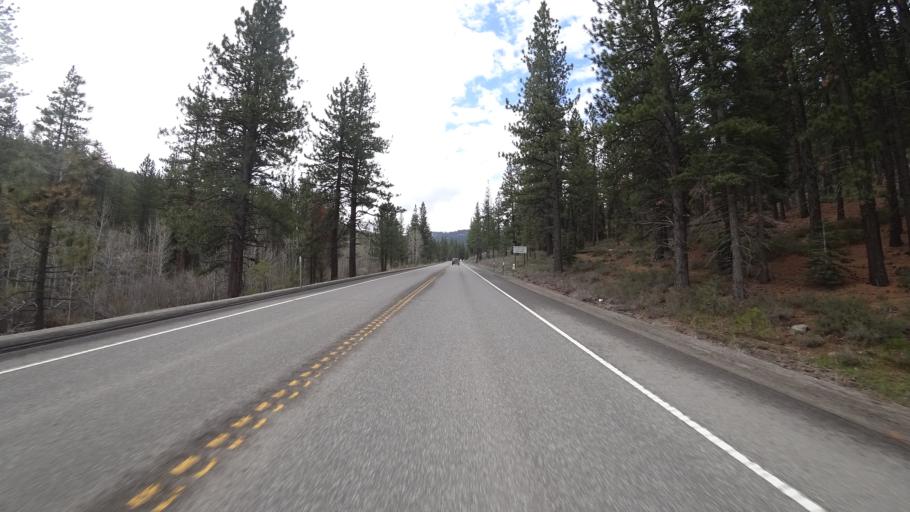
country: US
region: California
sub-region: Placer County
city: Tahoe Vista
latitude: 39.2949
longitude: -120.1044
